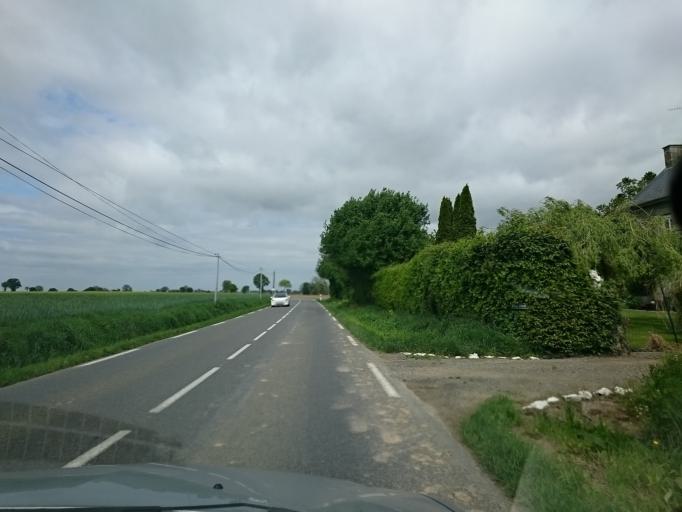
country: FR
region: Lower Normandy
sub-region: Departement de la Manche
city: Saint-James
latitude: 48.5488
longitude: -1.3918
